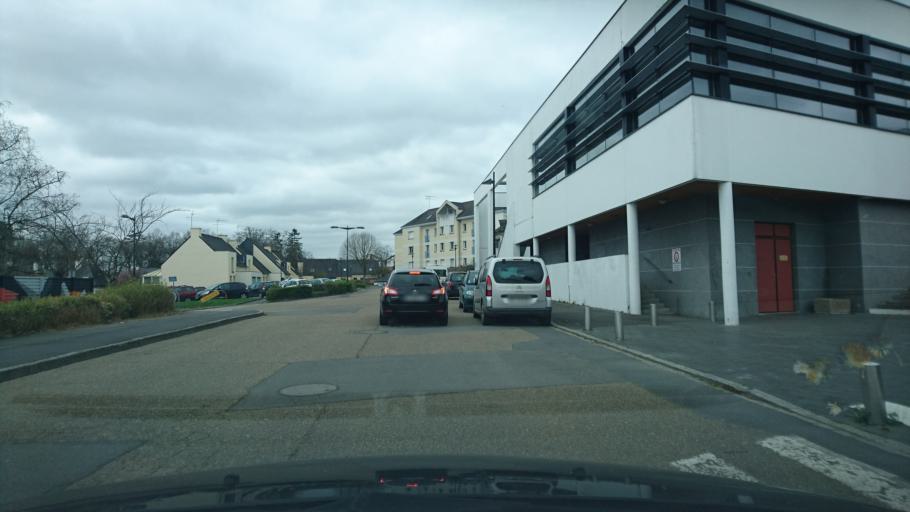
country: FR
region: Brittany
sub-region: Departement d'Ille-et-Vilaine
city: Bruz
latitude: 48.0226
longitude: -1.7443
